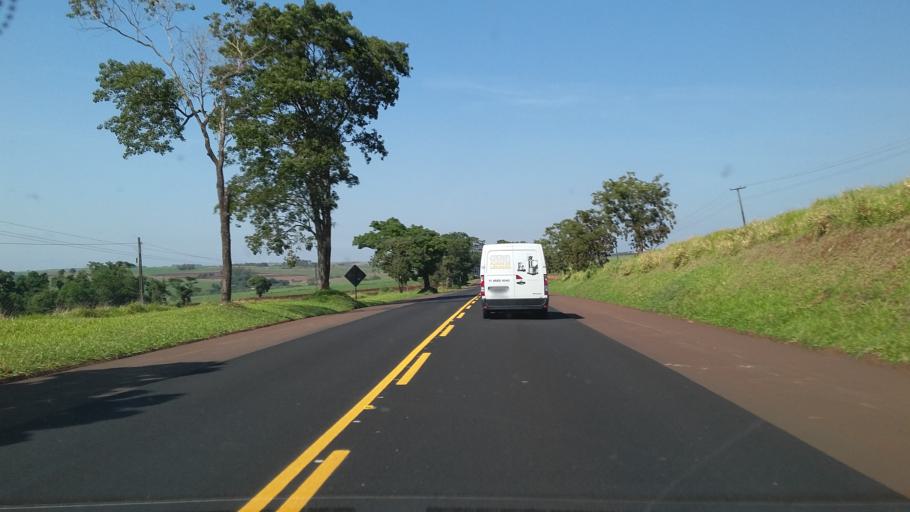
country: BR
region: Parana
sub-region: Bandeirantes
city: Bandeirantes
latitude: -23.1354
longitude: -50.4783
